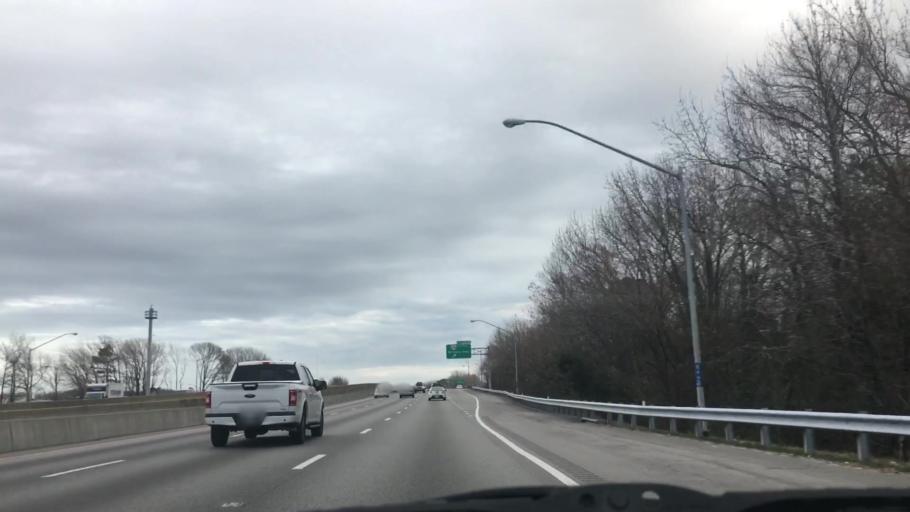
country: US
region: Virginia
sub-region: City of Norfolk
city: Norfolk
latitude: 36.8829
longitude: -76.2182
